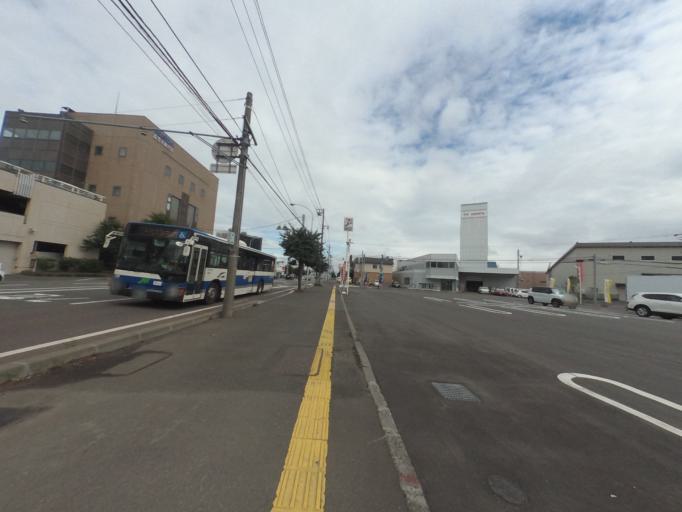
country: JP
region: Hokkaido
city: Sapporo
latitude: 43.0630
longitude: 141.3831
